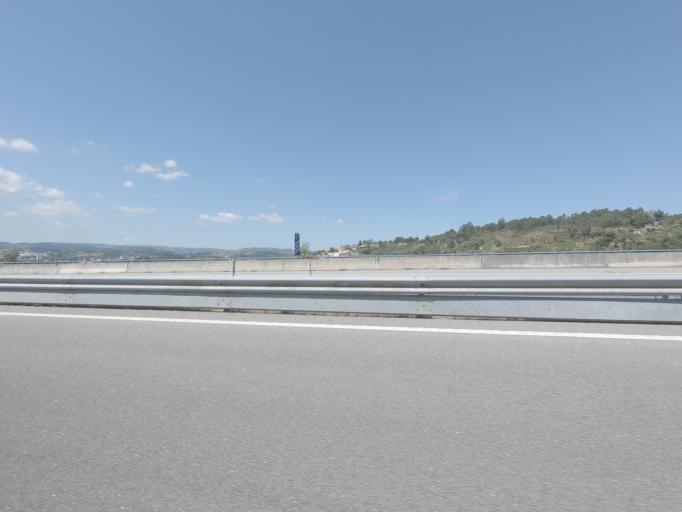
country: PT
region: Porto
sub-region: Amarante
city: Amarante
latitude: 41.2600
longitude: -8.0635
